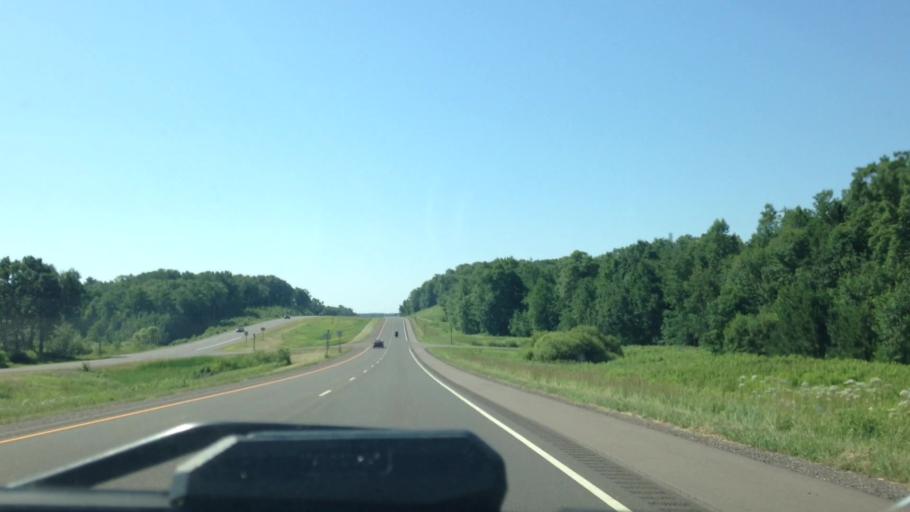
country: US
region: Wisconsin
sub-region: Washburn County
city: Spooner
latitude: 45.9999
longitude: -91.8324
